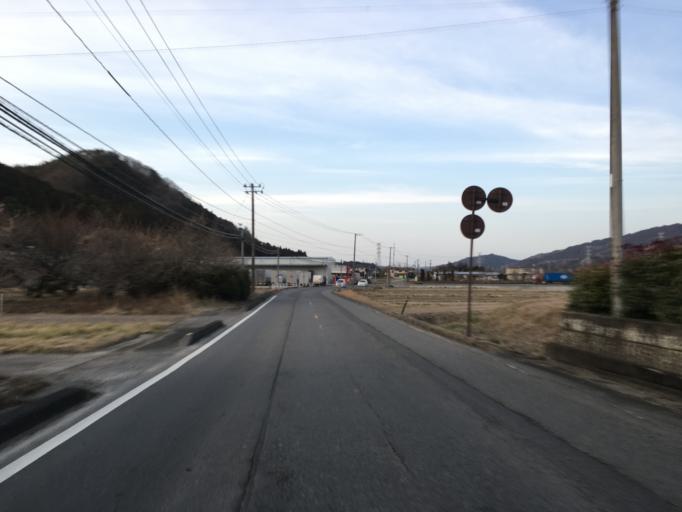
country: JP
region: Ibaraki
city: Daigo
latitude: 36.9128
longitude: 140.4080
